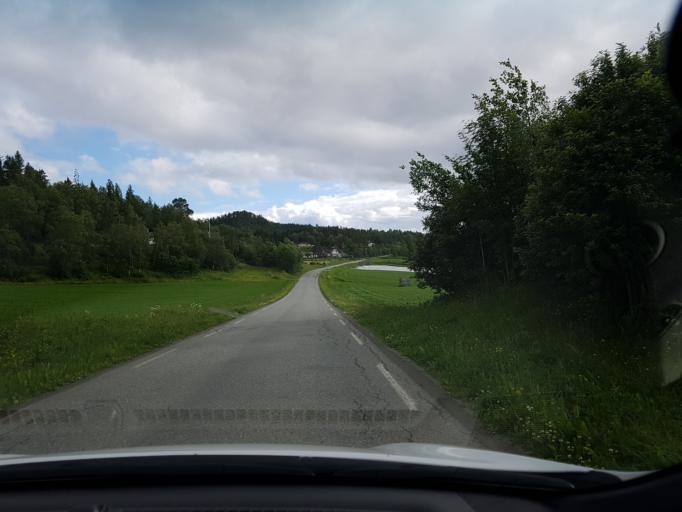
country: NO
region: Nord-Trondelag
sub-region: Frosta
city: Frosta
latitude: 63.6264
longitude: 10.7651
